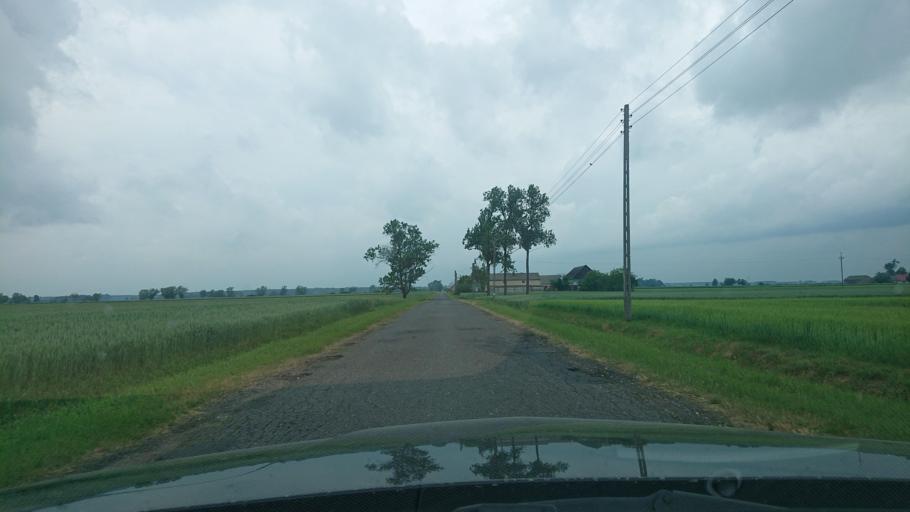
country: PL
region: Greater Poland Voivodeship
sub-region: Powiat gnieznienski
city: Czerniejewo
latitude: 52.4557
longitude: 17.5395
